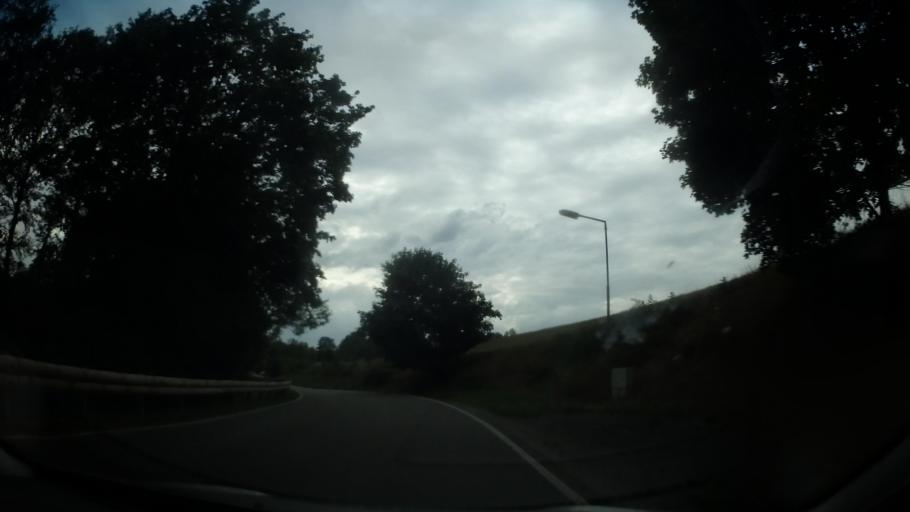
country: CZ
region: Pardubicky
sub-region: Okres Chrudim
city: Nasavrky
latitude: 49.8023
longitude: 15.7701
